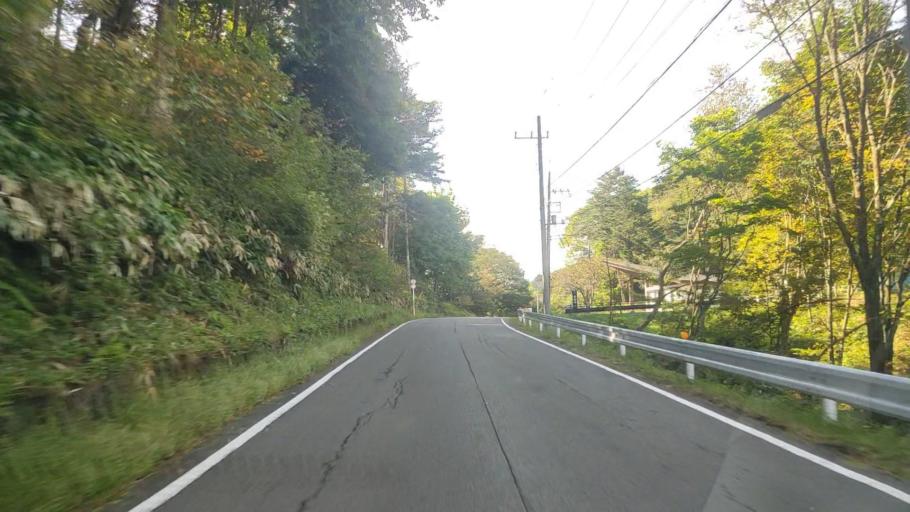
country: JP
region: Gunma
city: Nakanojomachi
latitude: 36.6034
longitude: 138.6845
